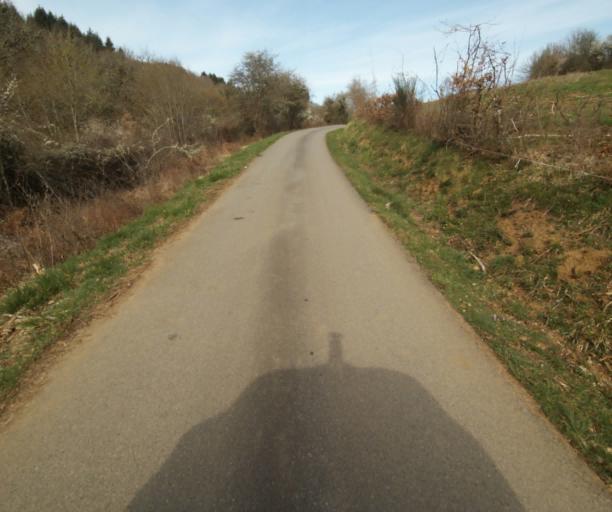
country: FR
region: Limousin
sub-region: Departement de la Correze
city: Correze
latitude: 45.4142
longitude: 1.7956
